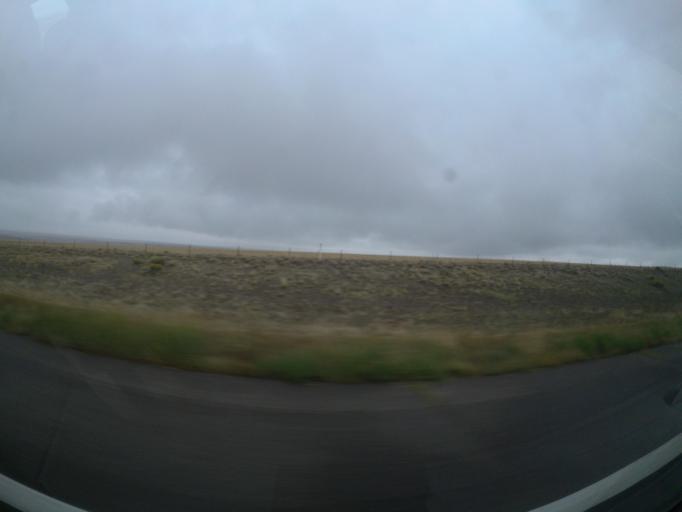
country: US
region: Colorado
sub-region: Arapahoe County
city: Byers
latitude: 39.7332
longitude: -103.9000
